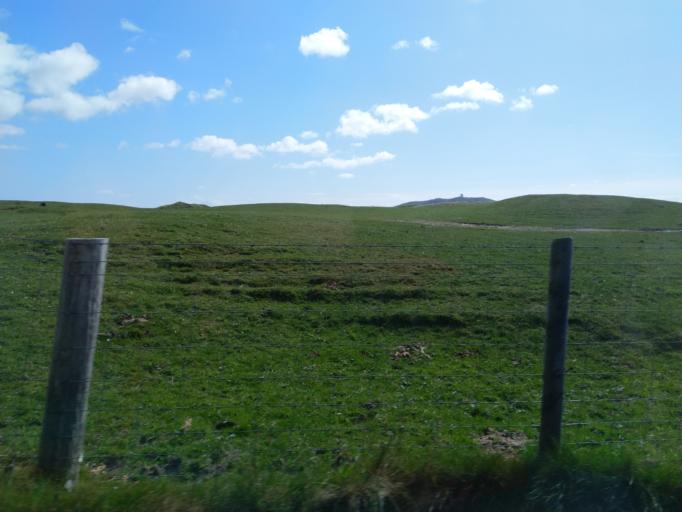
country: GB
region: Scotland
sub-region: Eilean Siar
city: Barra
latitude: 56.4851
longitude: -6.8946
